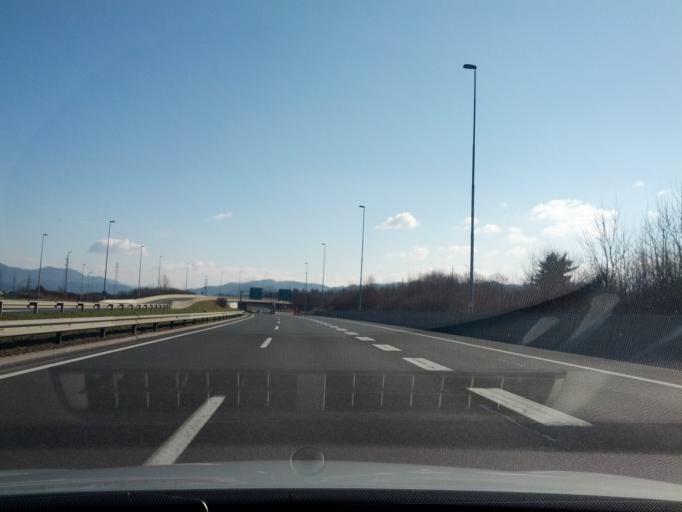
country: SI
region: Dol pri Ljubljani
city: Dol pri Ljubljani
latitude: 46.0675
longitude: 14.5692
